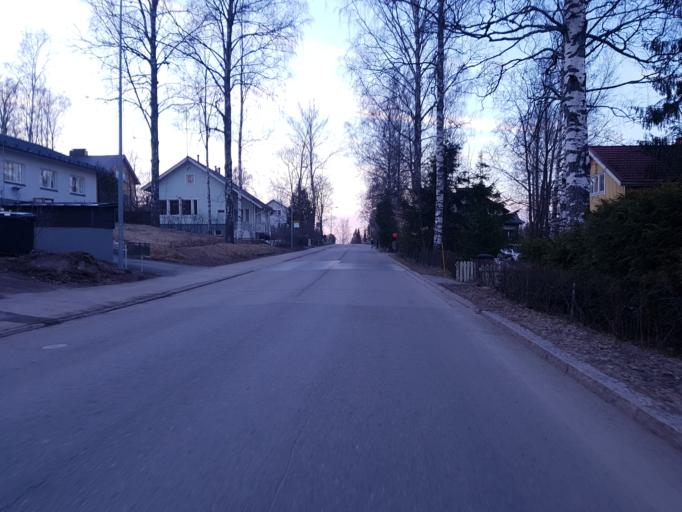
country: FI
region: Uusimaa
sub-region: Helsinki
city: Helsinki
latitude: 60.2598
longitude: 24.9536
